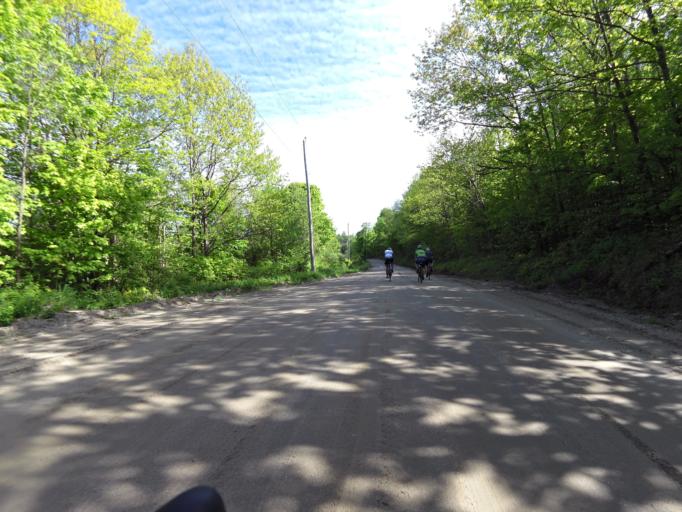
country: CA
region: Quebec
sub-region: Outaouais
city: Wakefield
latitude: 45.6824
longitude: -75.8914
